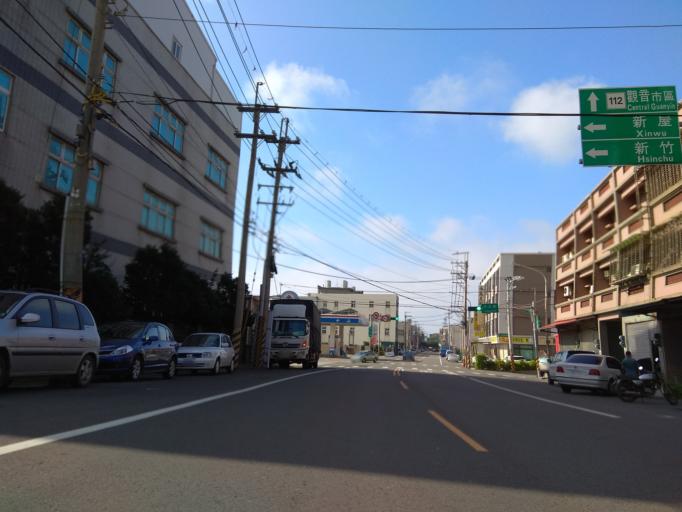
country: TW
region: Taiwan
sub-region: Hsinchu
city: Zhubei
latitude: 25.0347
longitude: 121.0862
